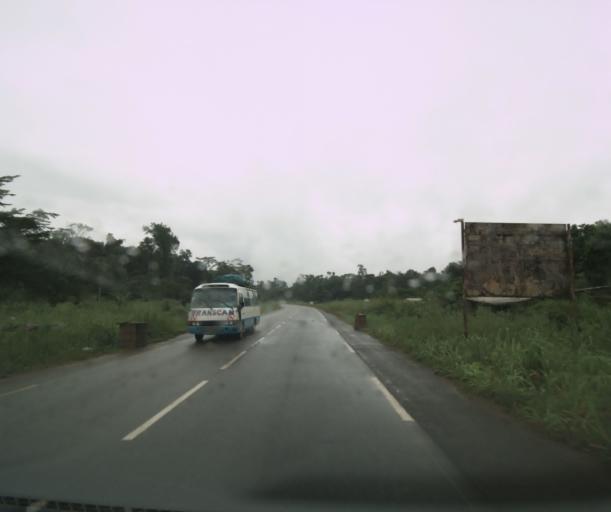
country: CM
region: Littoral
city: Edea
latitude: 3.4647
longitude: 10.1307
